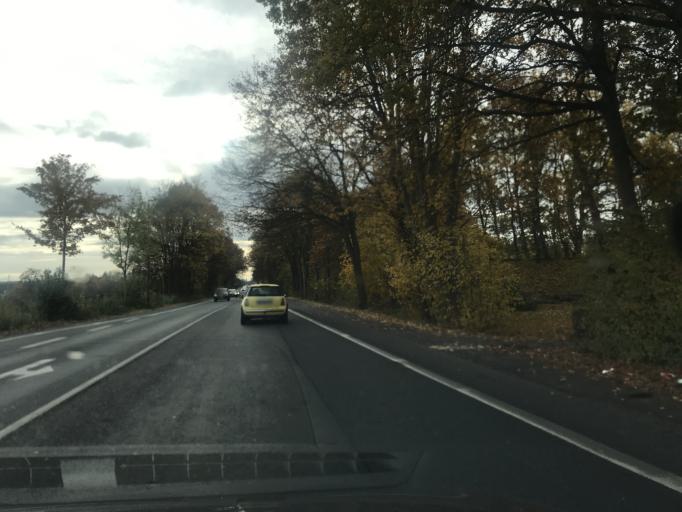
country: DE
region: North Rhine-Westphalia
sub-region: Regierungsbezirk Arnsberg
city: Hamm
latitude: 51.6531
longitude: 7.8392
